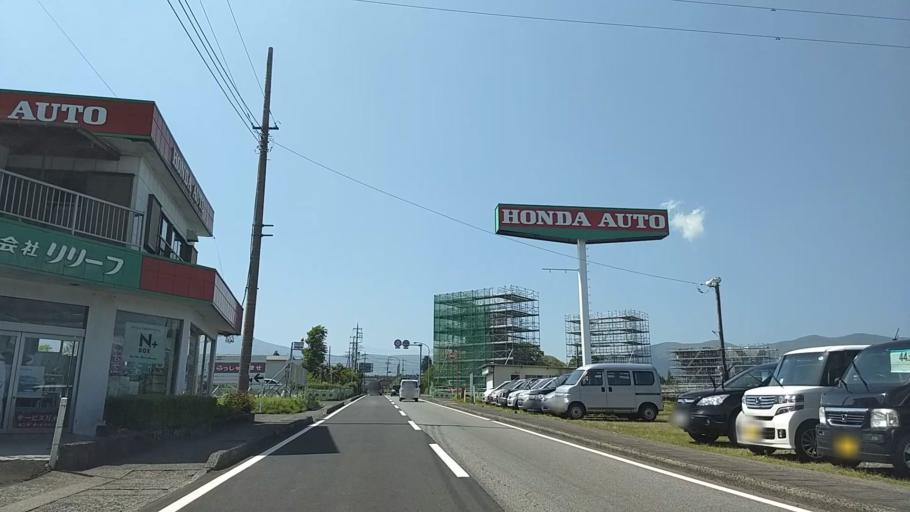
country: JP
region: Shizuoka
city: Gotemba
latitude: 35.3150
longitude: 138.9189
